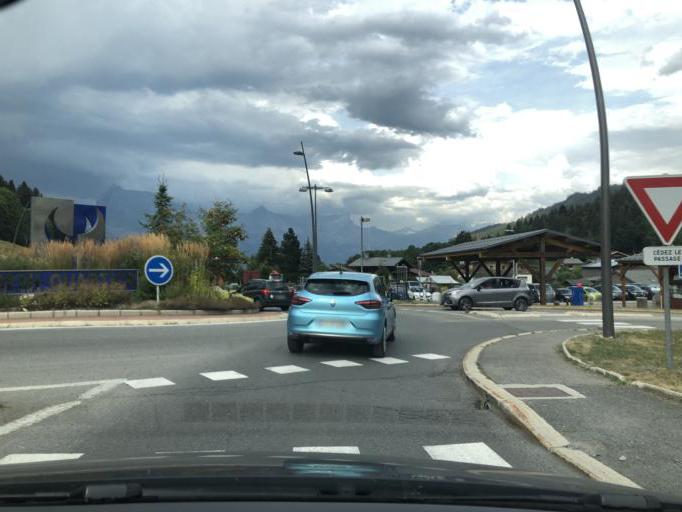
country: FR
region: Rhone-Alpes
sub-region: Departement de la Haute-Savoie
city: Megeve
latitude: 45.8713
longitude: 6.6300
